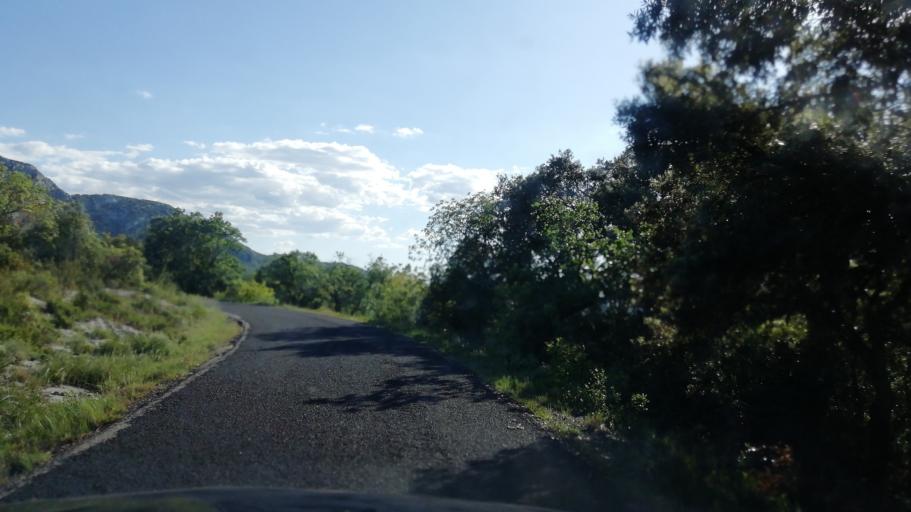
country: FR
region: Languedoc-Roussillon
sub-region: Departement de l'Herault
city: Saint-Mathieu-de-Treviers
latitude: 43.7923
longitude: 3.8089
